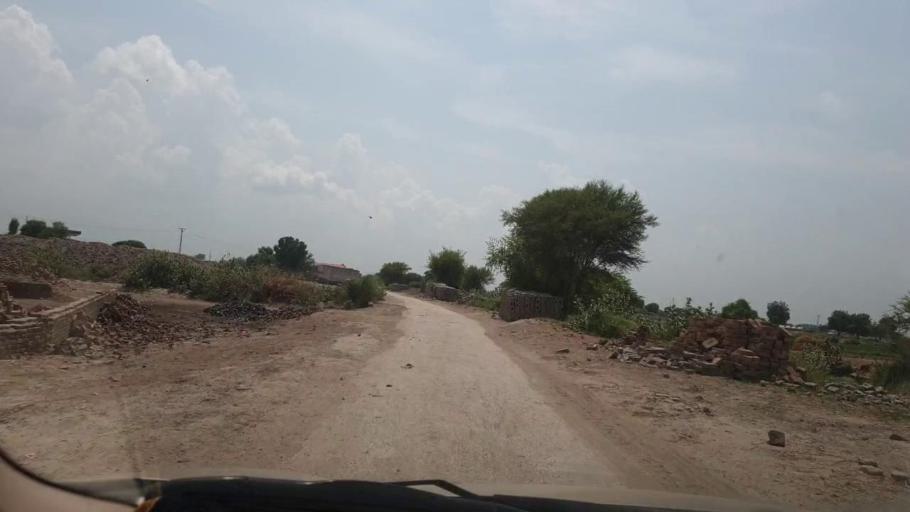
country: PK
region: Sindh
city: Larkana
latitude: 27.5804
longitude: 68.1137
